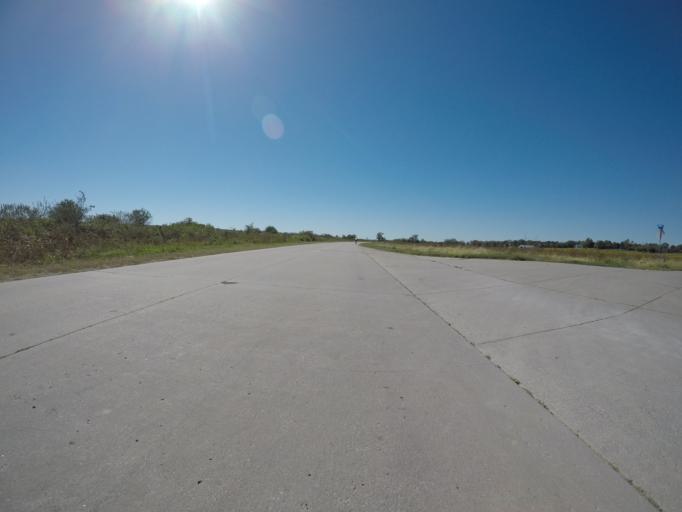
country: US
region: Kansas
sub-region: Wyandotte County
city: Bonner Springs
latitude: 39.0216
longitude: -94.9011
